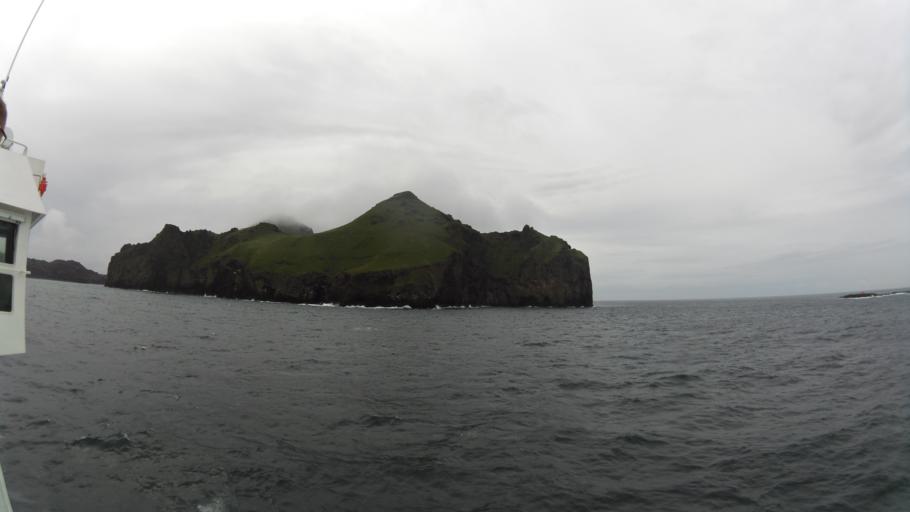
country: IS
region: South
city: Vestmannaeyjar
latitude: 63.4530
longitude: -20.2311
